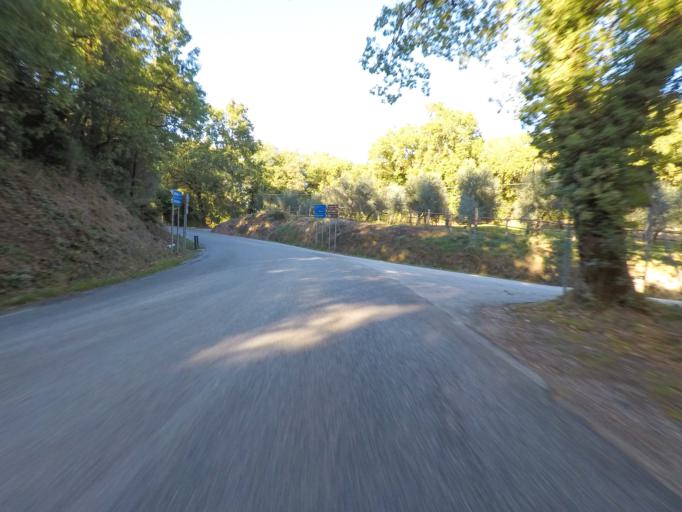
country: IT
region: Tuscany
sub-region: Provincia di Siena
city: Belverde
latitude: 43.4100
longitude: 11.3522
